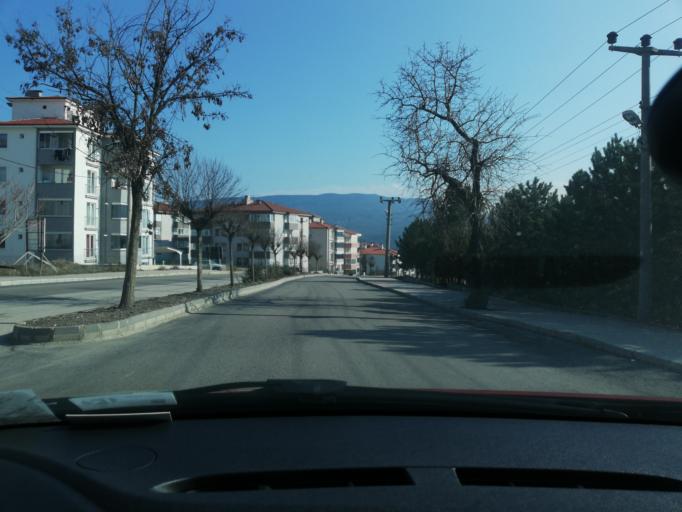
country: TR
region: Karabuk
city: Safranbolu
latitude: 41.2339
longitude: 32.6673
